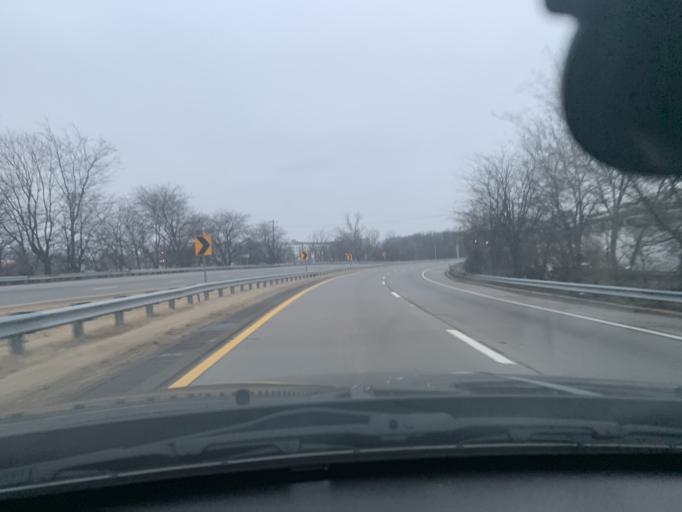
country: US
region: Tennessee
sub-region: Davidson County
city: Nashville
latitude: 36.1796
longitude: -86.7630
